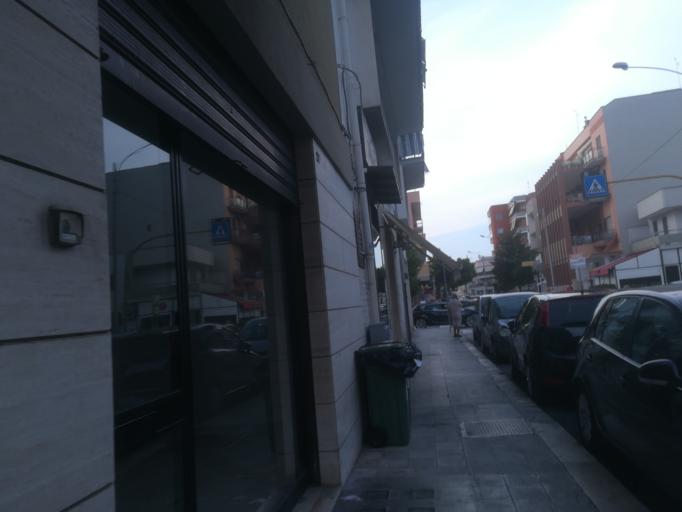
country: IT
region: Apulia
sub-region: Provincia di Bari
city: Monopoli
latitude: 40.9474
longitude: 17.3038
